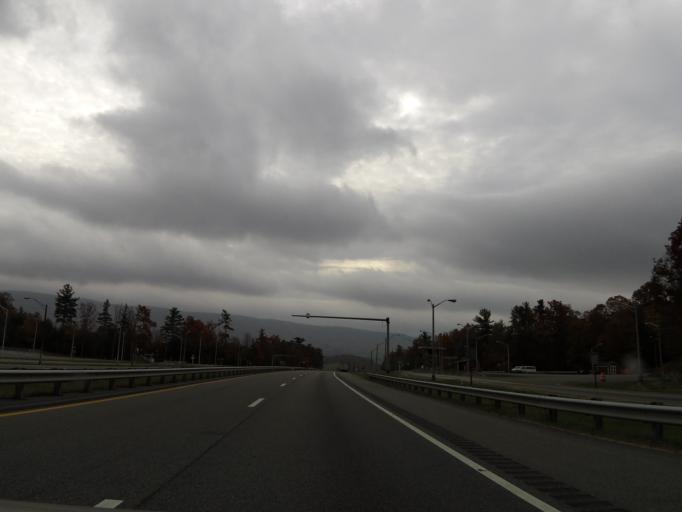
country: US
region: Virginia
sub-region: Bland County
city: Bland
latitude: 37.0871
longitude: -81.1268
